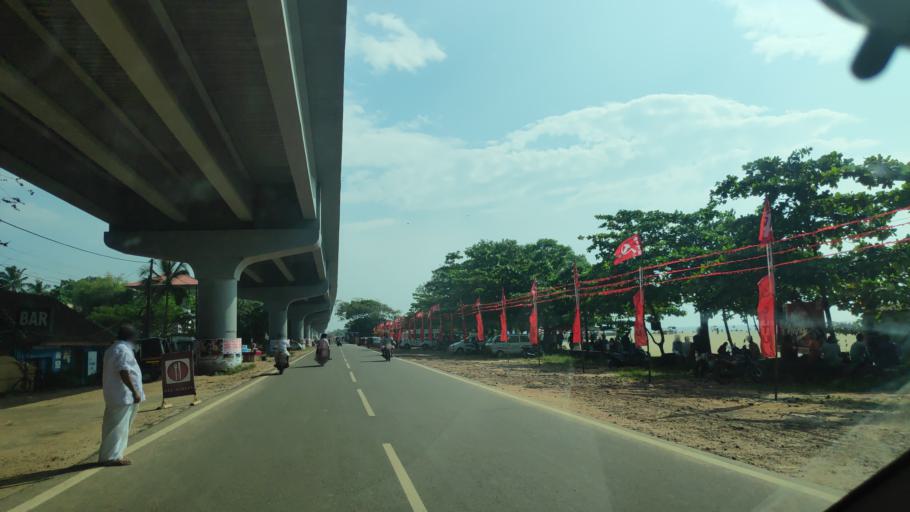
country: IN
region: Kerala
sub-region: Alappuzha
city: Alleppey
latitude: 9.4941
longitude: 76.3184
